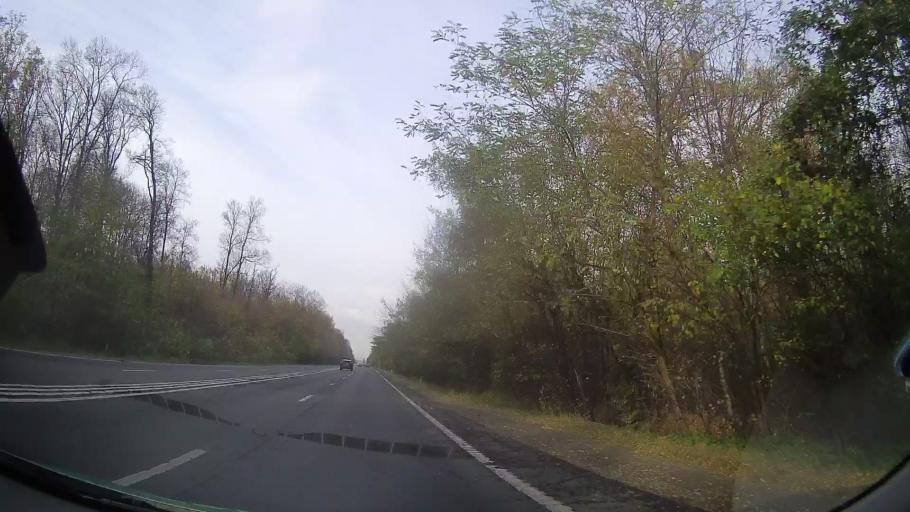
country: RO
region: Prahova
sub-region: Comuna Puchenii Mari
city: Puchenii Mari
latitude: 44.8407
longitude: 26.0787
